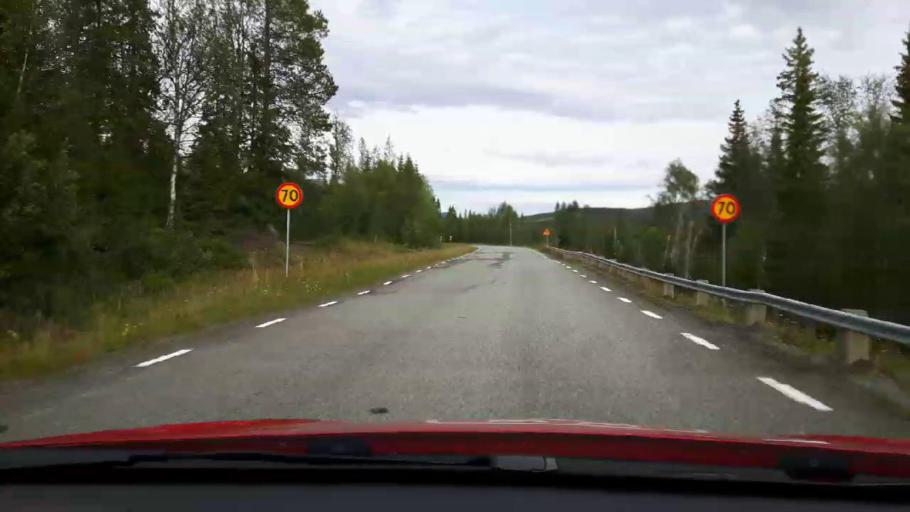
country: SE
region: Jaemtland
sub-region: Are Kommun
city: Are
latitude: 63.7416
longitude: 13.0788
